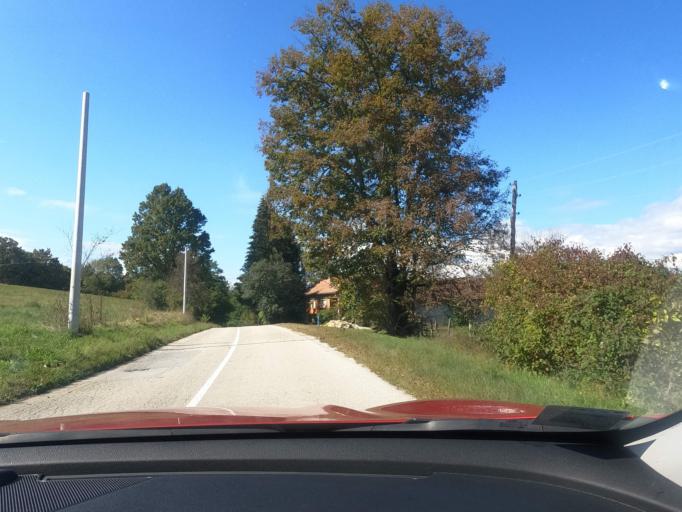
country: BA
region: Federation of Bosnia and Herzegovina
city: Vrnograc
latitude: 45.2360
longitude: 15.9311
